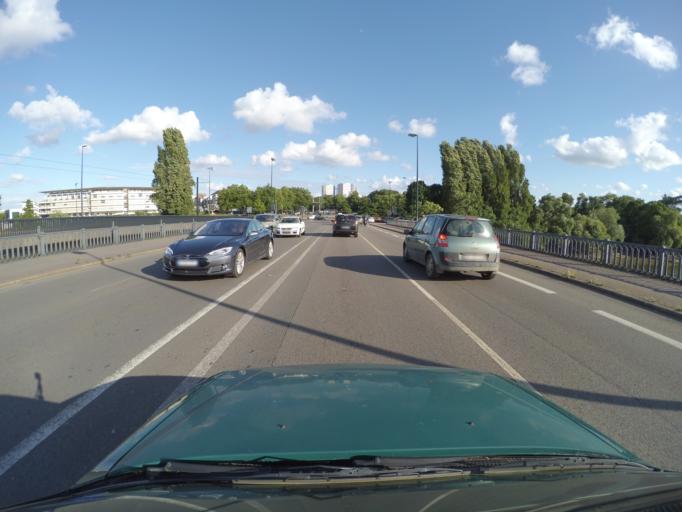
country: FR
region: Pays de la Loire
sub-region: Departement de la Loire-Atlantique
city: Reze
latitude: 47.1986
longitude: -1.5430
